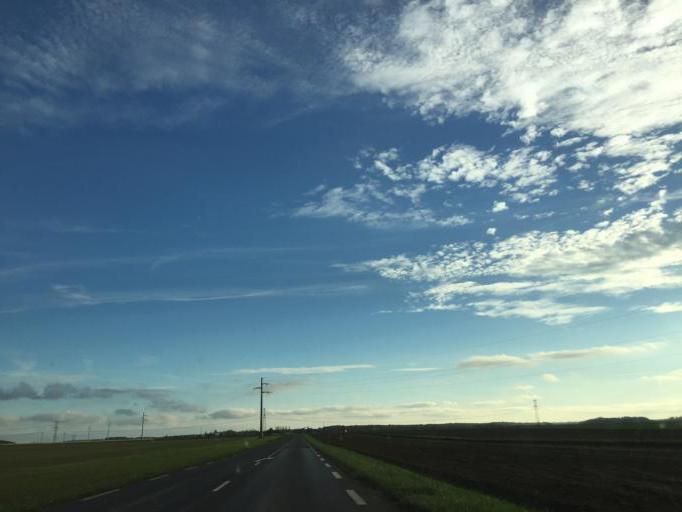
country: FR
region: Ile-de-France
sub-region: Departement de Seine-et-Marne
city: Jouy-le-Chatel
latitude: 48.6156
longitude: 3.1028
